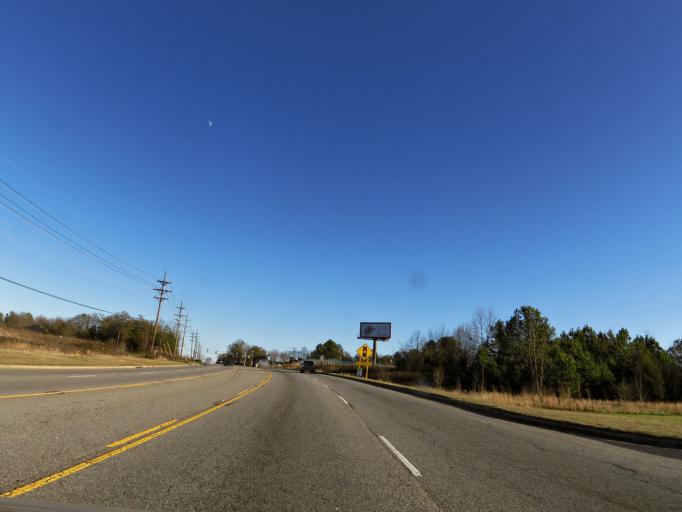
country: US
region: South Carolina
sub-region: Spartanburg County
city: Wellford
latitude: 34.8963
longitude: -82.0905
